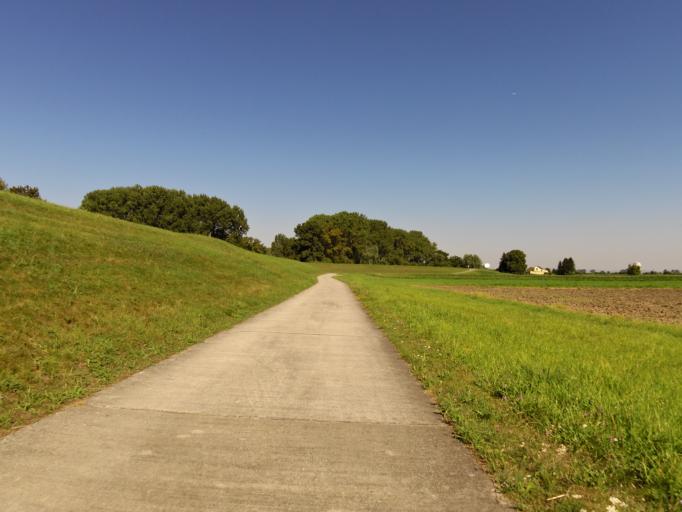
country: DE
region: Rheinland-Pfalz
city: Oppenheim
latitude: 49.8462
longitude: 8.4009
